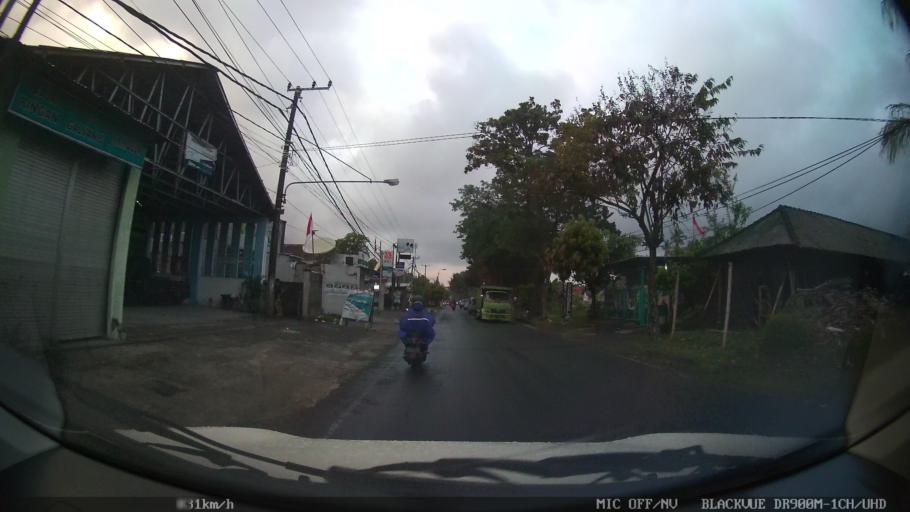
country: ID
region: Bali
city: Banjar Batur
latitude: -8.5974
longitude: 115.2148
